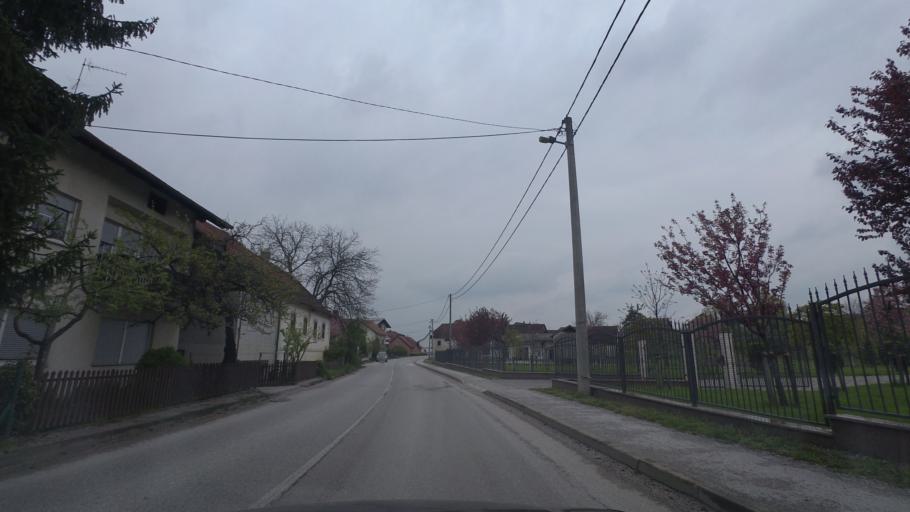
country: HR
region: Karlovacka
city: Ozalj
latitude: 45.6504
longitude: 15.5206
